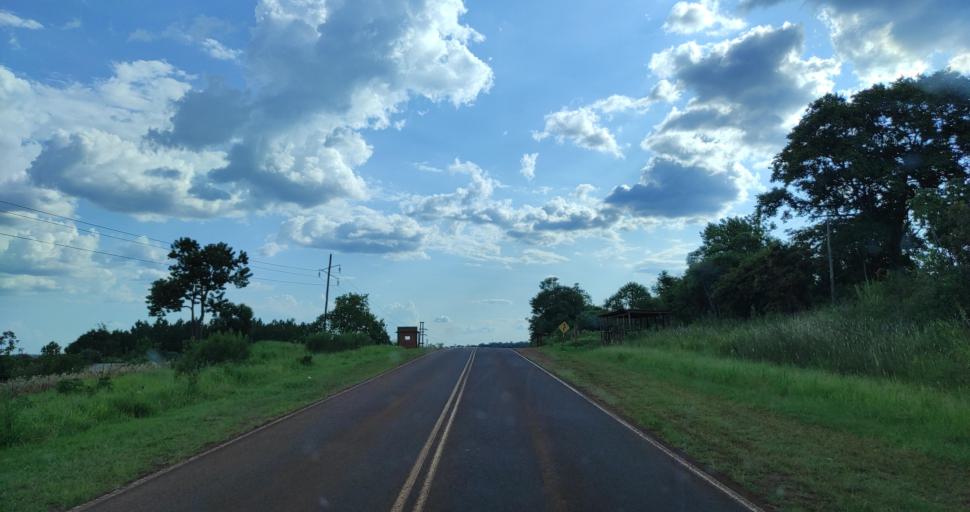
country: AR
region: Misiones
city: San Vicente
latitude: -26.3386
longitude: -54.1773
